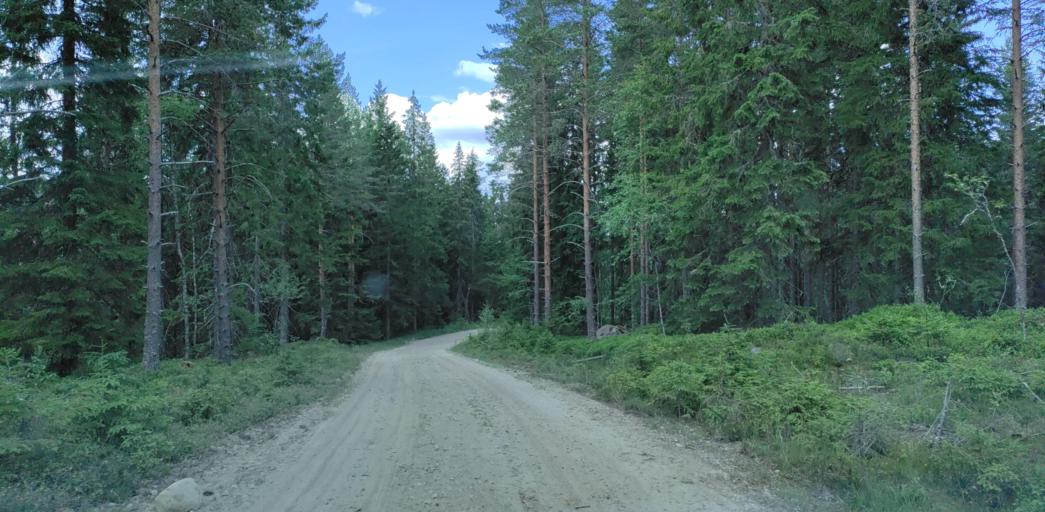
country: SE
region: Vaermland
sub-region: Hagfors Kommun
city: Ekshaerad
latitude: 60.0740
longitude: 13.3456
